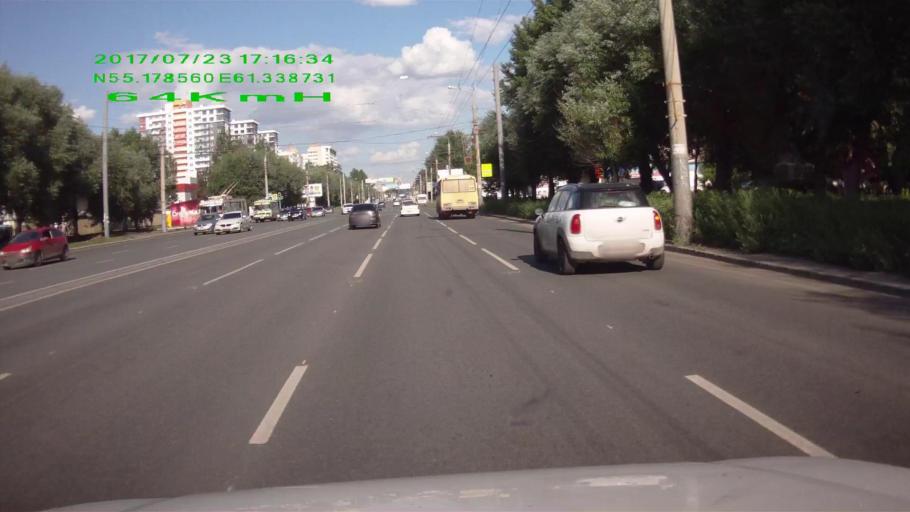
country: RU
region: Chelyabinsk
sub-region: Gorod Chelyabinsk
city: Chelyabinsk
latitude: 55.1786
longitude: 61.3394
